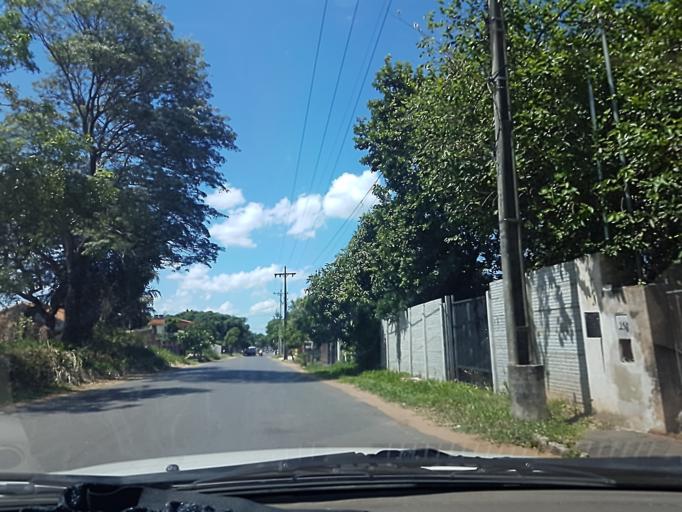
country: PY
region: Central
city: San Lorenzo
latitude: -25.2601
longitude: -57.4952
